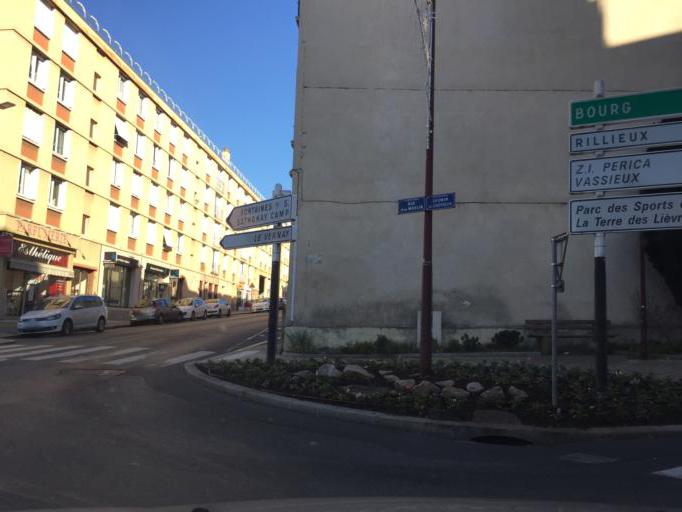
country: FR
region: Rhone-Alpes
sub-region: Departement du Rhone
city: Caluire-et-Cuire
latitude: 45.8006
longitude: 4.8488
